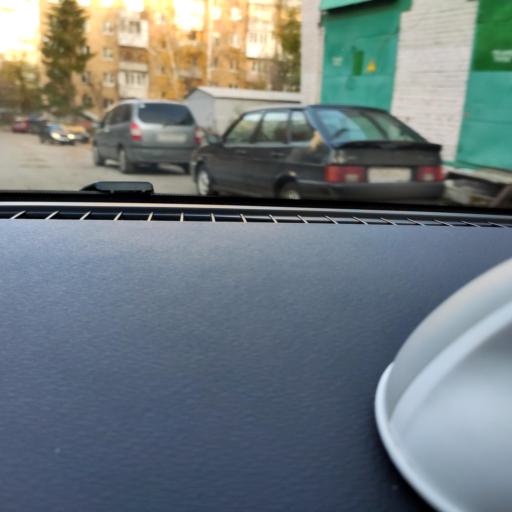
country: RU
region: Samara
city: Samara
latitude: 53.2391
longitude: 50.2236
